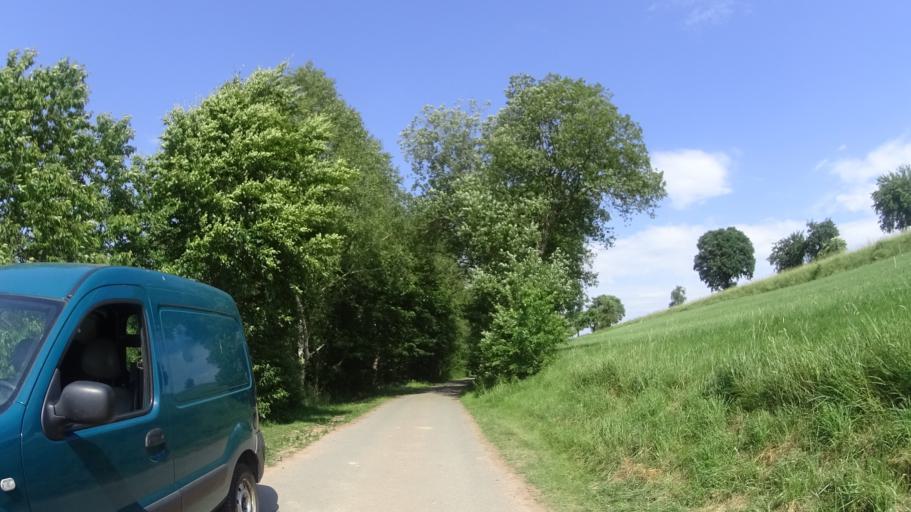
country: DE
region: Hesse
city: Rosenthal
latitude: 50.9705
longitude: 8.8510
